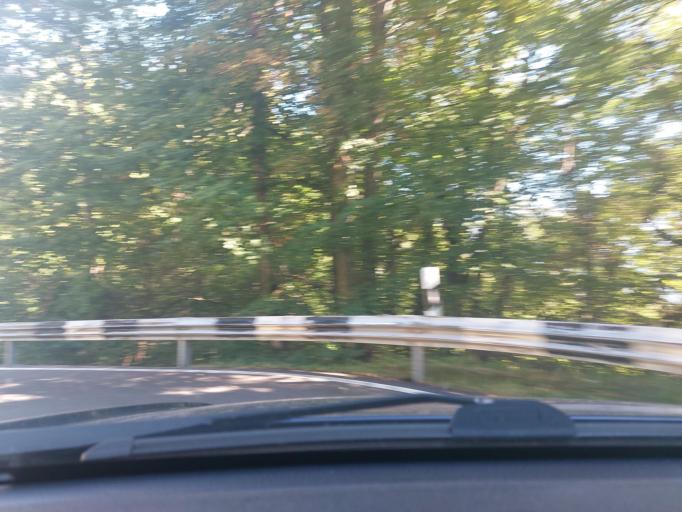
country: CH
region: Vaud
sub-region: Aigle District
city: Aigle
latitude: 46.3446
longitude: 6.9584
